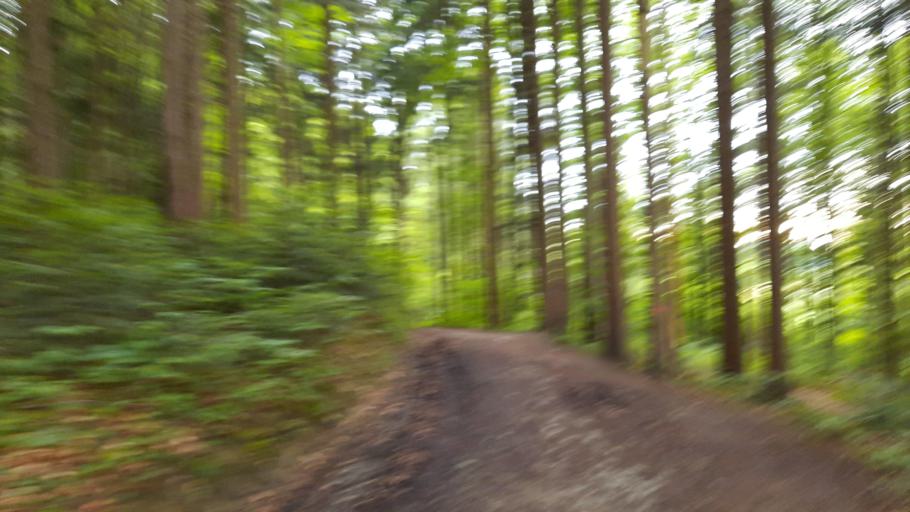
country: DE
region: Bavaria
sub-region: Upper Bavaria
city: Vagen
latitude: 47.8477
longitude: 11.8500
